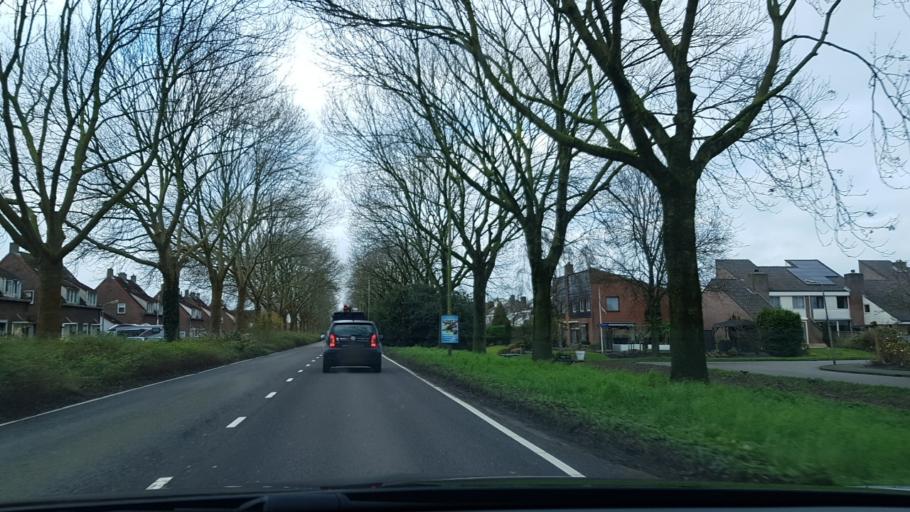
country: NL
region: South Holland
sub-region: Gemeente Kaag en Braassem
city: Oude Wetering
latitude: 52.2040
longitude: 4.6296
